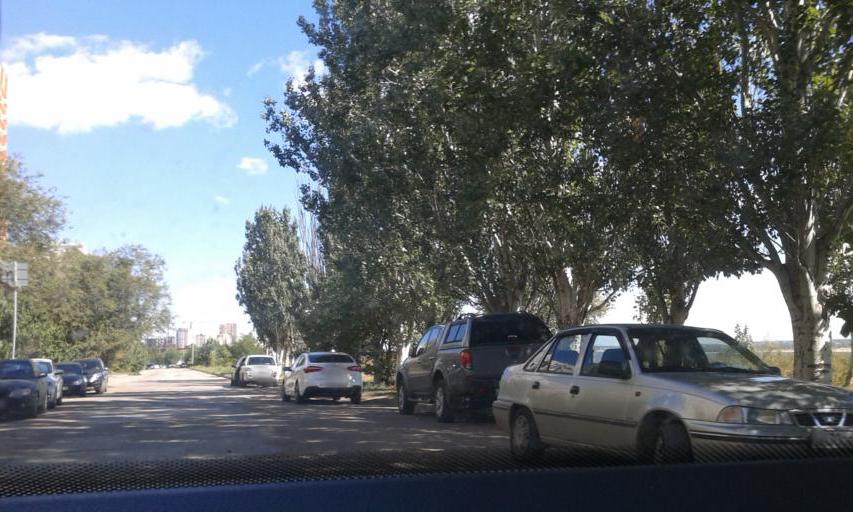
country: RU
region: Volgograd
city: Volgograd
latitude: 48.6737
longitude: 44.4767
